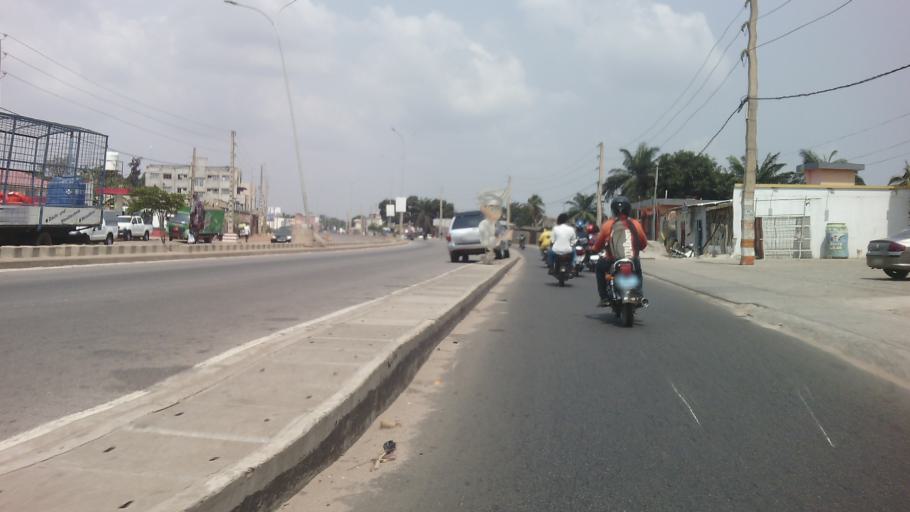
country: BJ
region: Atlantique
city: Abomey-Calavi
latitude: 6.4298
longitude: 2.3507
